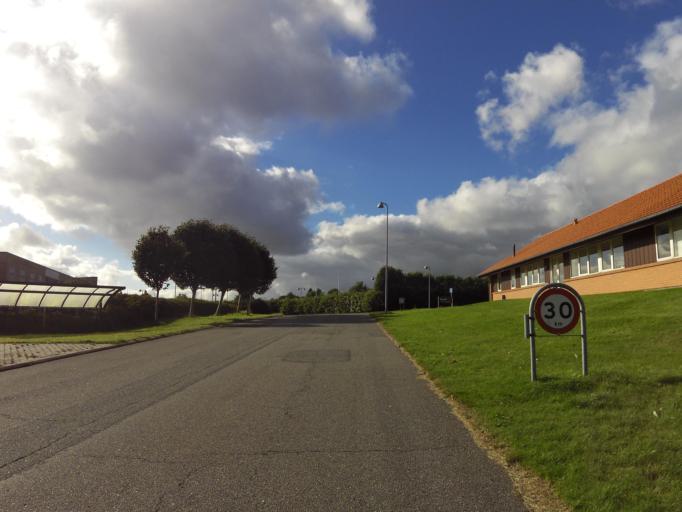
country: DK
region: South Denmark
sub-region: Tonder Kommune
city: Toftlund
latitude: 55.1800
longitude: 9.0666
